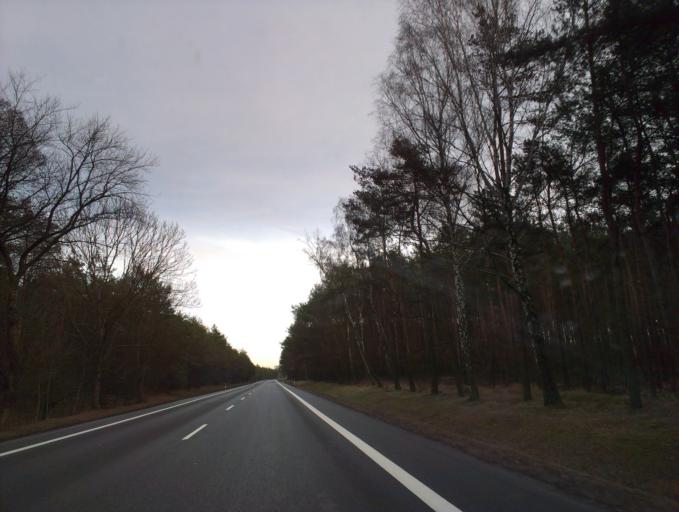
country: PL
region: Masovian Voivodeship
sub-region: Powiat sierpecki
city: Szczutowo
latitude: 52.8955
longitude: 19.5476
